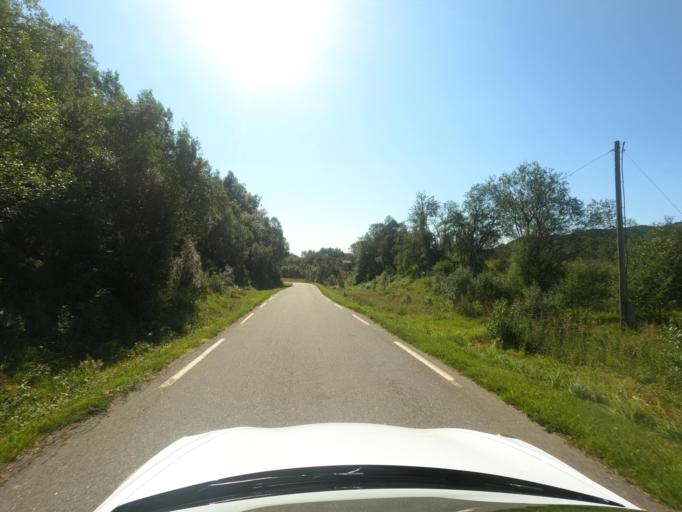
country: NO
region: Nordland
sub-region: Hadsel
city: Stokmarknes
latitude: 68.3047
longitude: 15.0936
